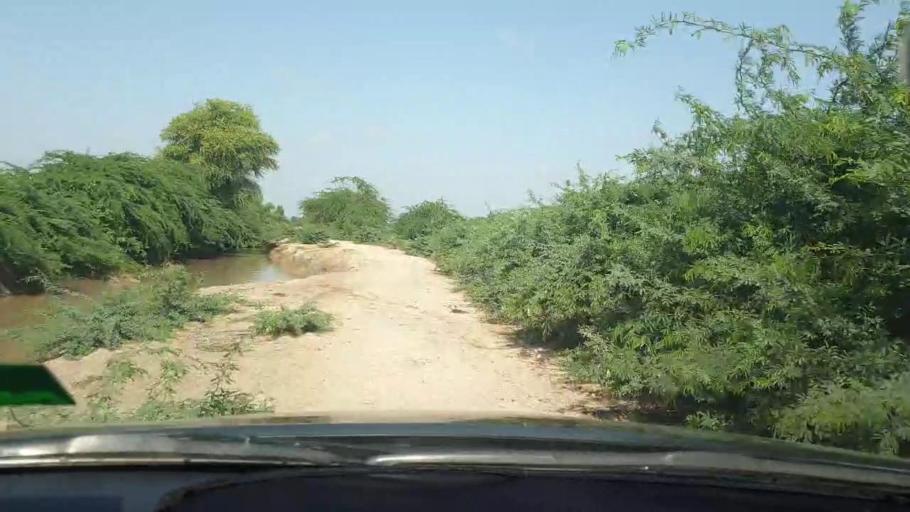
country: PK
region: Sindh
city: Tando Bago
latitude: 24.7808
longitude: 68.9441
